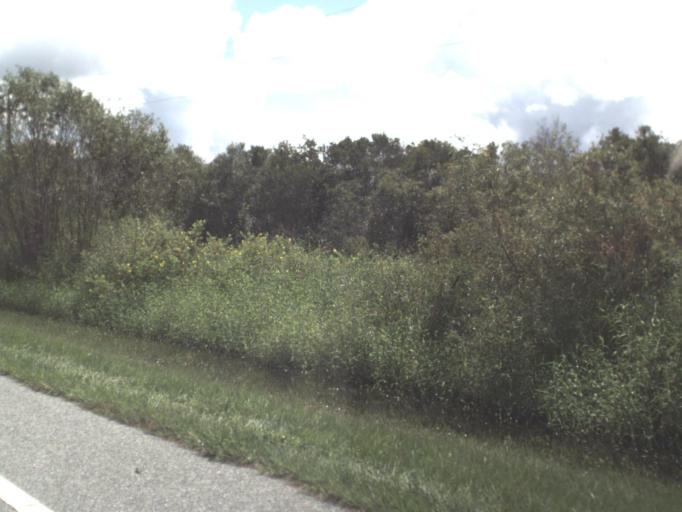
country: US
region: Florida
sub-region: DeSoto County
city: Arcadia
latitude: 27.3071
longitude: -82.0926
